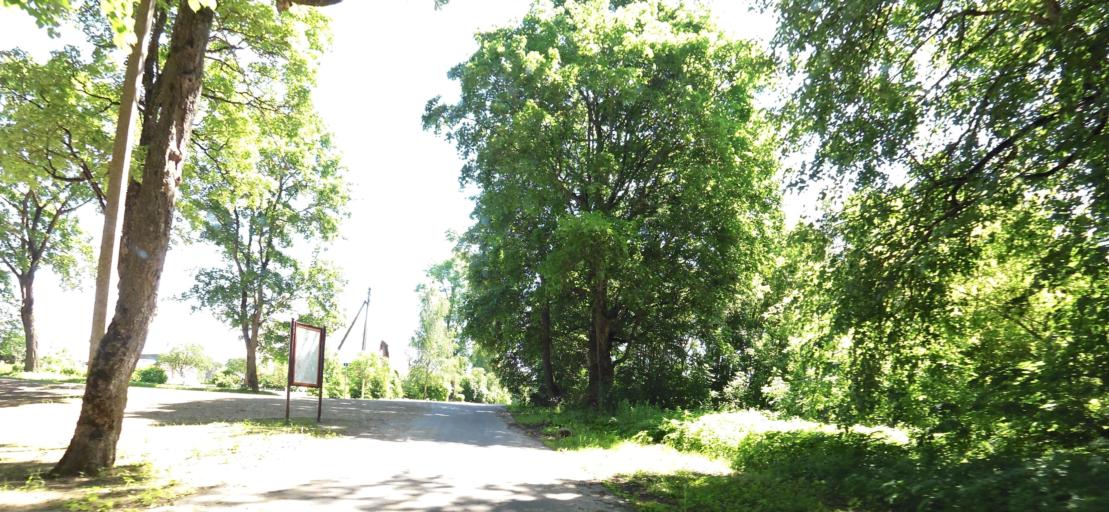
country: LT
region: Vilnius County
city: Pasilaiciai
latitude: 54.9848
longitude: 25.2237
